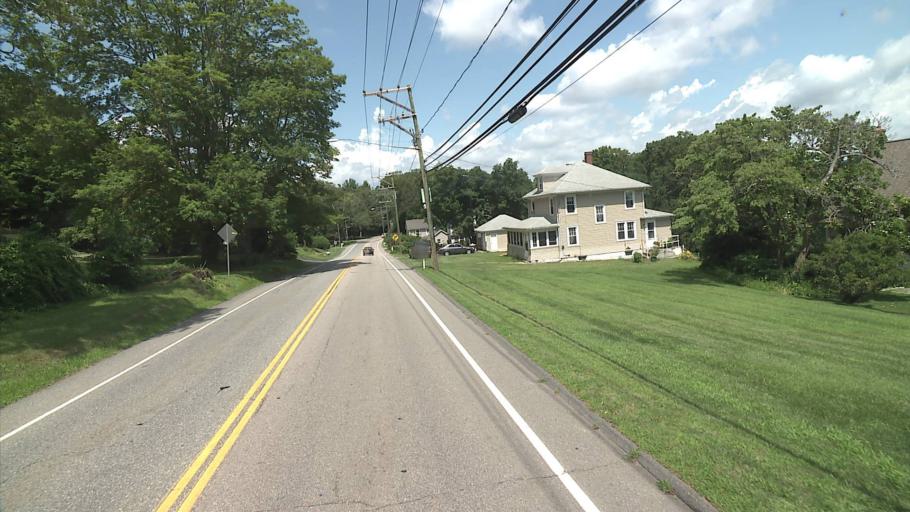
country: US
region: Connecticut
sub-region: Middlesex County
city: Chester Center
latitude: 41.3982
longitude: -72.4403
